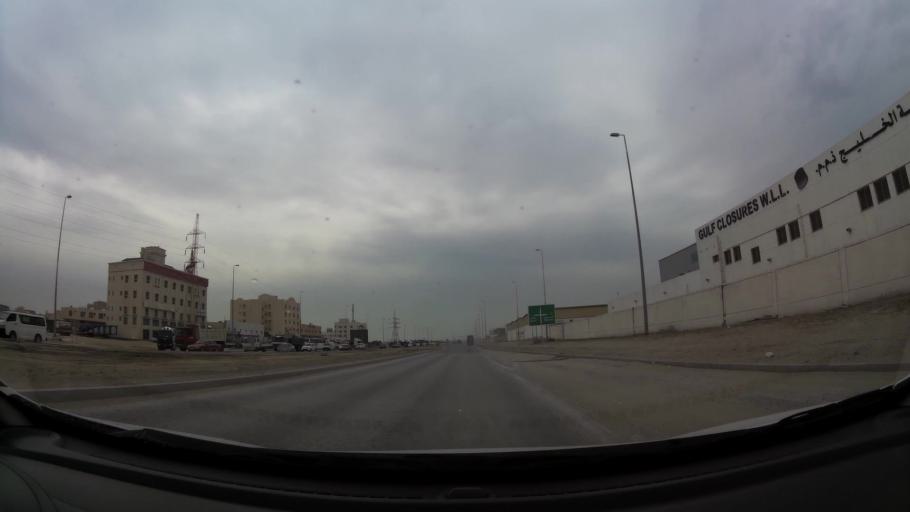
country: BH
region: Northern
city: Sitrah
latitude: 26.1754
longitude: 50.6038
